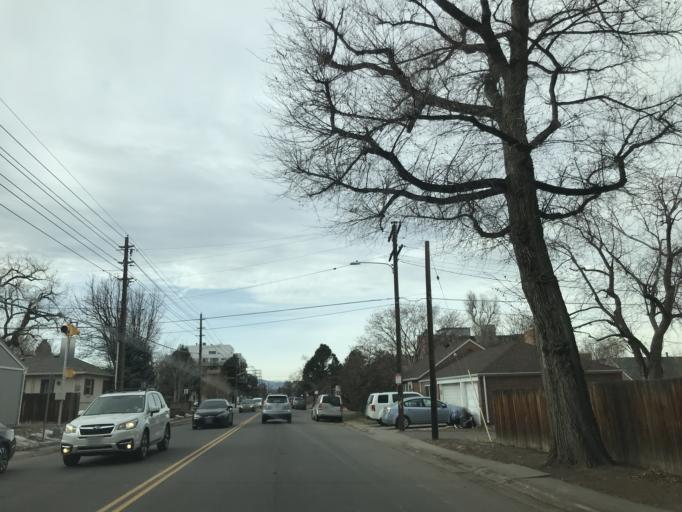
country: US
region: Colorado
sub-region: Arapahoe County
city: Glendale
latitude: 39.7293
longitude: -104.9296
